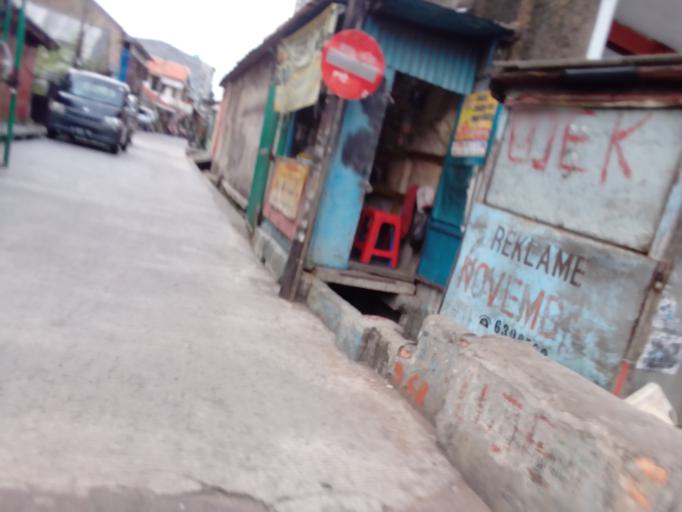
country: ID
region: Jakarta Raya
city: Jakarta
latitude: -6.1659
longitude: 106.8052
